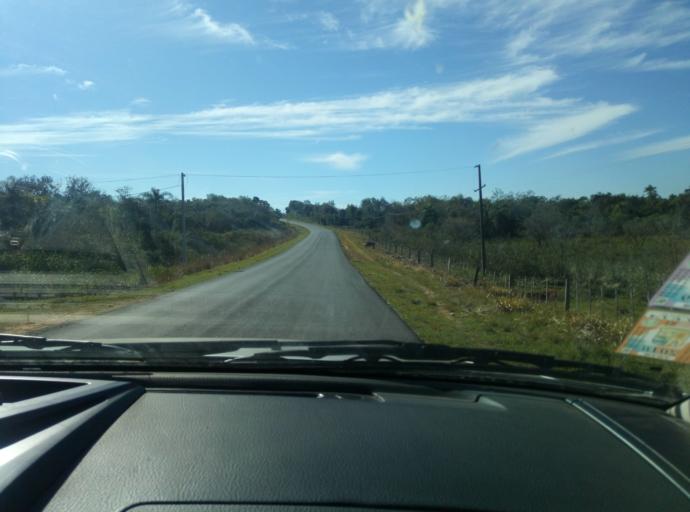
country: PY
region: Caaguazu
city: Carayao
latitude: -25.1727
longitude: -56.3133
